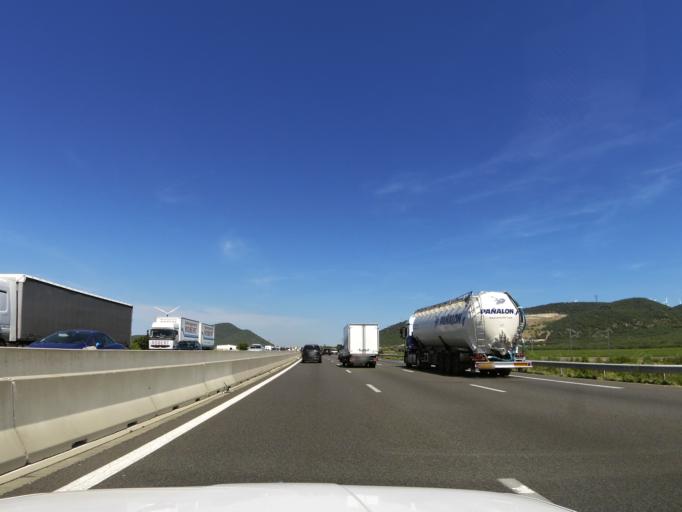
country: FR
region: Rhone-Alpes
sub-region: Departement de la Drome
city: Donzere
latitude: 44.4417
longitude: 4.7518
